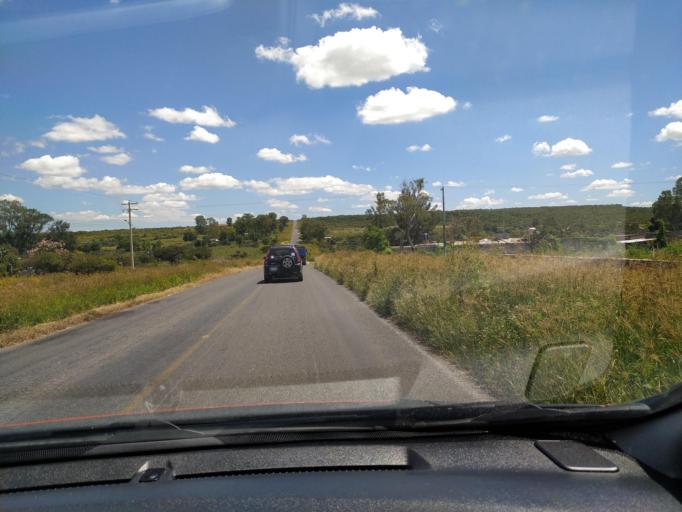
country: MX
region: Jalisco
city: San Diego de Alejandria
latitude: 21.0071
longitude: -102.0348
